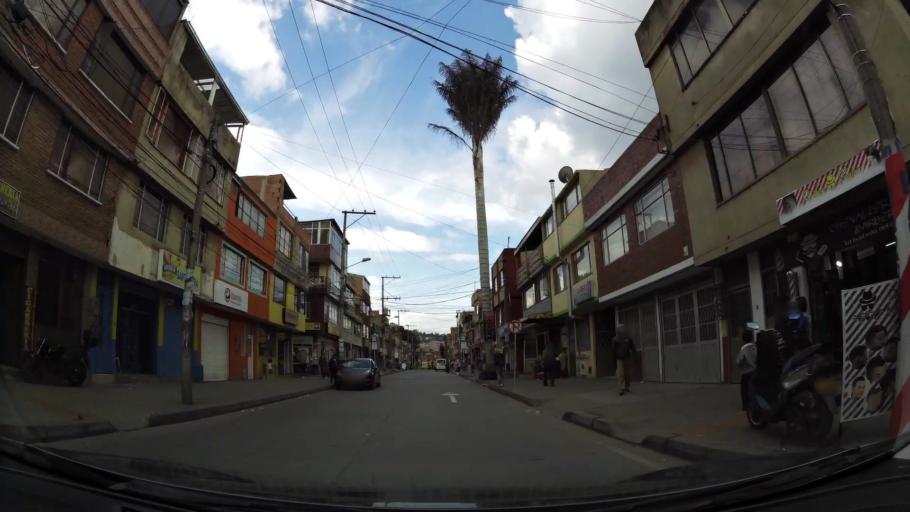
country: CO
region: Cundinamarca
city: Cota
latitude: 4.7301
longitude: -74.0992
